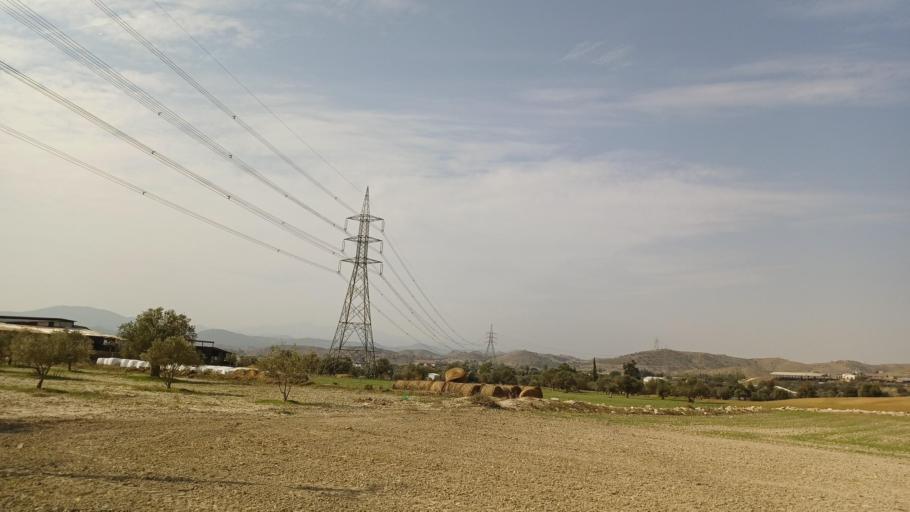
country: CY
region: Lefkosia
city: Lympia
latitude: 34.9829
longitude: 33.4532
